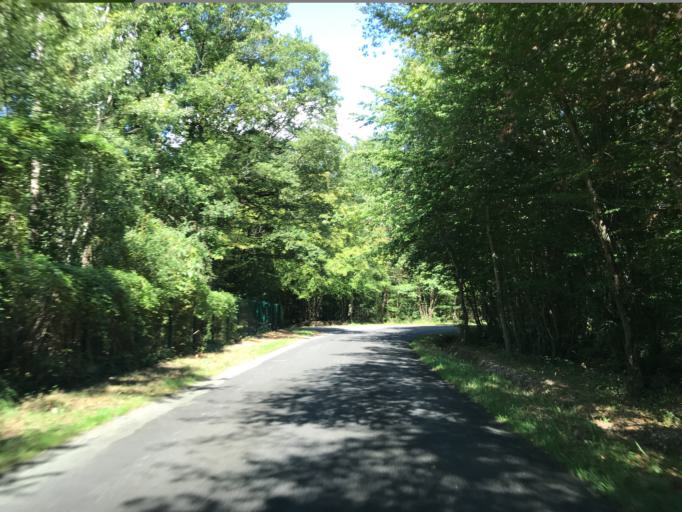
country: FR
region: Haute-Normandie
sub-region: Departement de l'Eure
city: La Chapelle-Reanville
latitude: 49.0847
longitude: 1.3947
